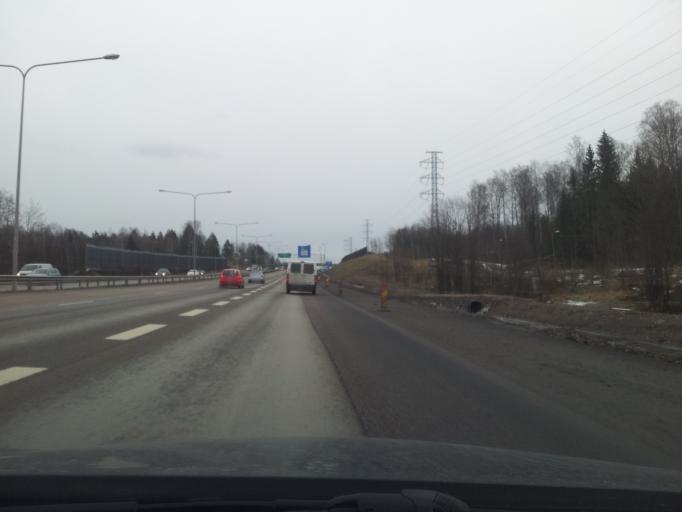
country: FI
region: Uusimaa
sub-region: Helsinki
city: Kilo
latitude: 60.2077
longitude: 24.7940
